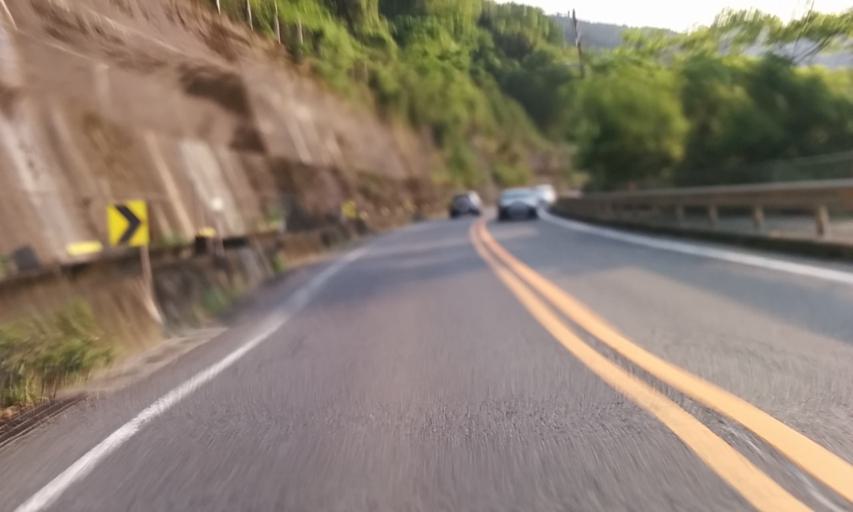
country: JP
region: Ehime
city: Saijo
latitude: 33.8530
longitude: 133.0109
